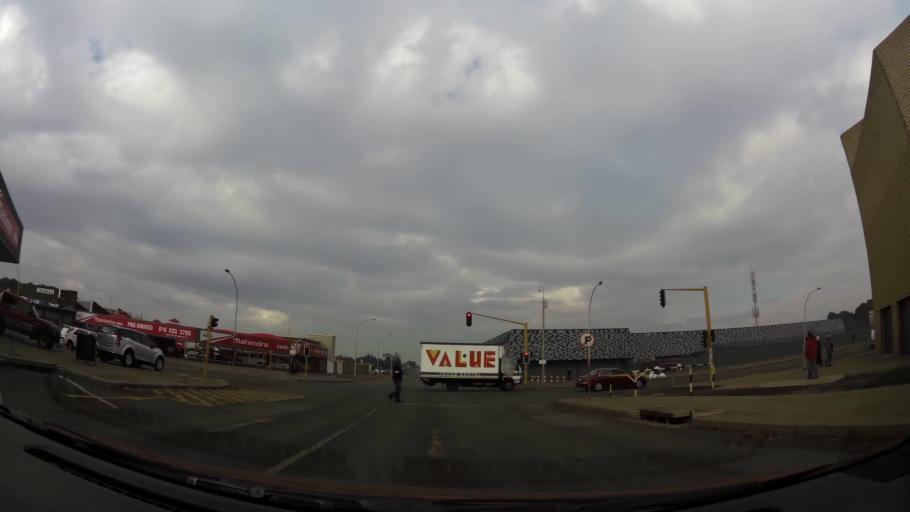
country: ZA
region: Gauteng
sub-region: Sedibeng District Municipality
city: Vanderbijlpark
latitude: -26.7000
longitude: 27.8389
